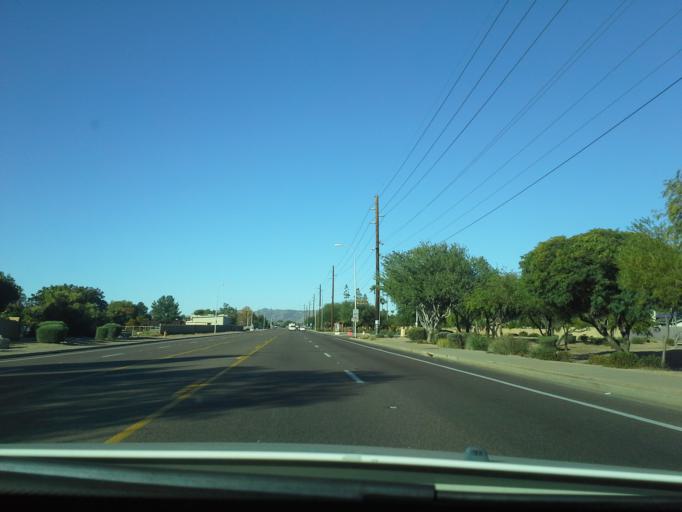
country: US
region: Arizona
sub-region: Maricopa County
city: San Carlos
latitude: 33.3495
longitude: -111.8845
